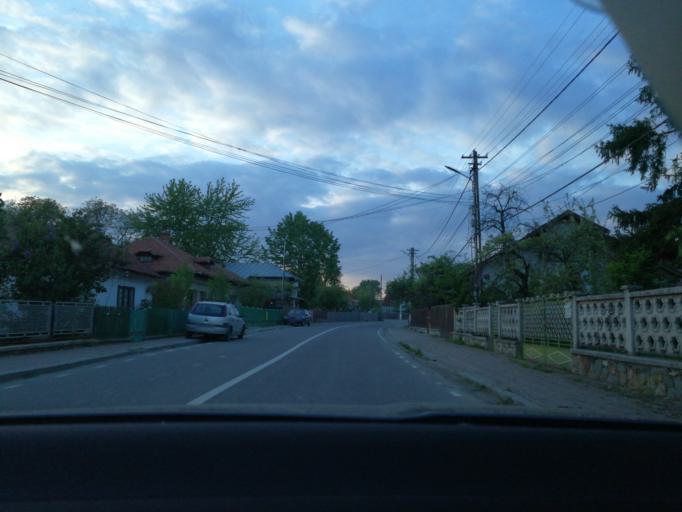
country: RO
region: Prahova
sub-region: Comuna Cornu
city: Cornu de Jos
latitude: 45.1481
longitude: 25.7075
